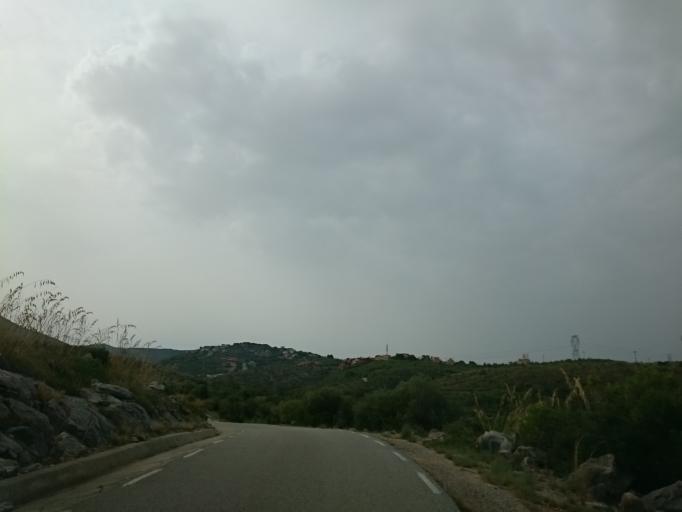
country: ES
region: Catalonia
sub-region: Provincia de Barcelona
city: Olivella
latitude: 41.3011
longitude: 1.8525
